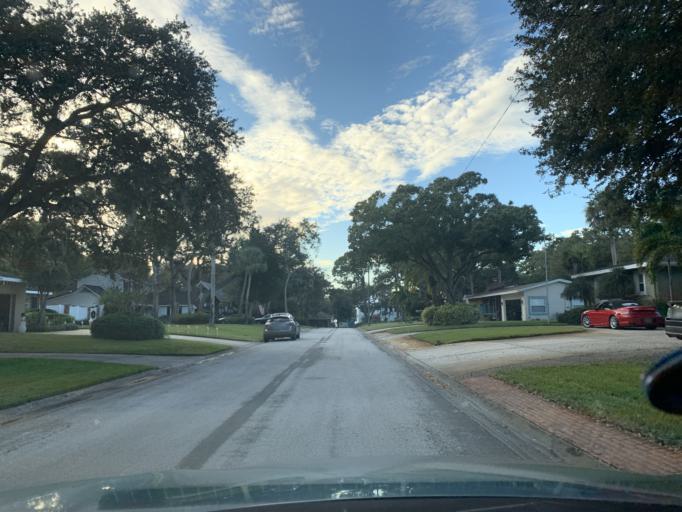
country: US
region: Florida
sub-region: Pinellas County
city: Bay Pines
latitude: 27.8057
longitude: -82.7554
